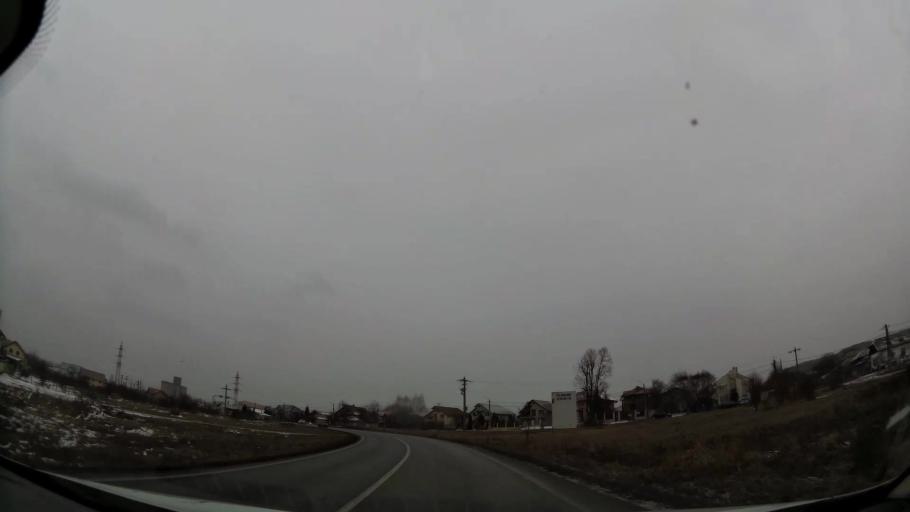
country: RO
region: Dambovita
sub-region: Comuna Aninoasa
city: Viforata
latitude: 44.9515
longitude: 25.4787
